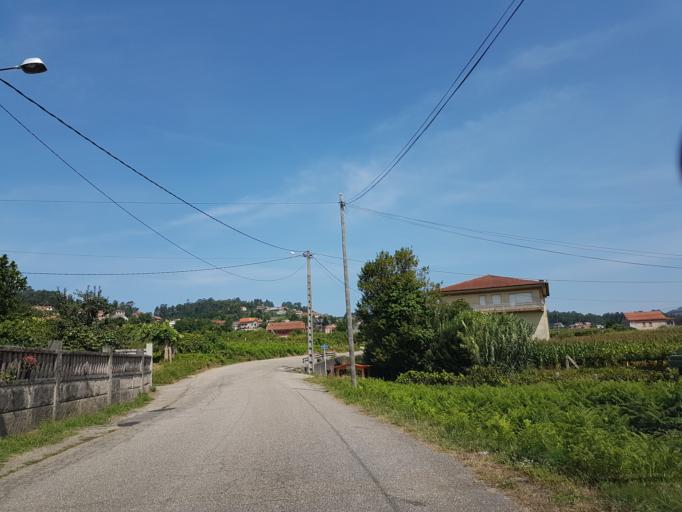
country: ES
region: Galicia
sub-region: Provincia de Pontevedra
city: Porrino
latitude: 42.2162
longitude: -8.6216
